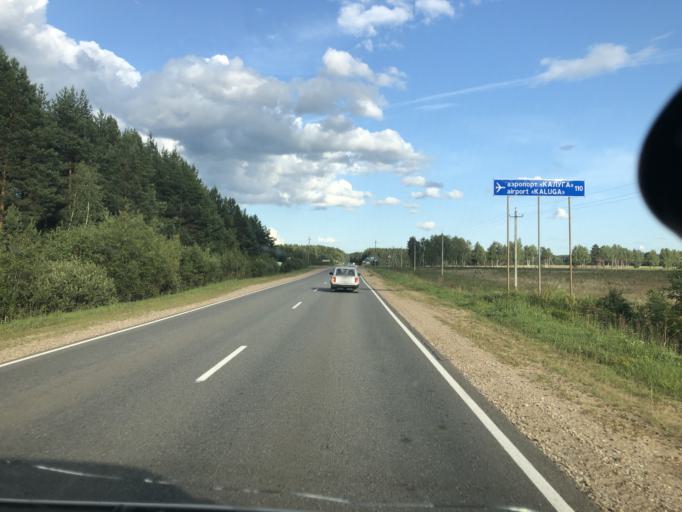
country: RU
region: Kaluga
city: Yukhnov
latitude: 54.7198
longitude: 35.2244
